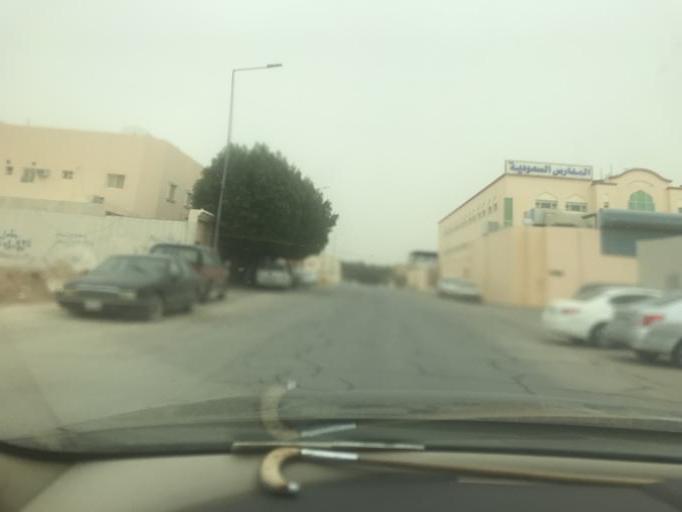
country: SA
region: Ar Riyad
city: Riyadh
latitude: 24.7293
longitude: 46.7896
